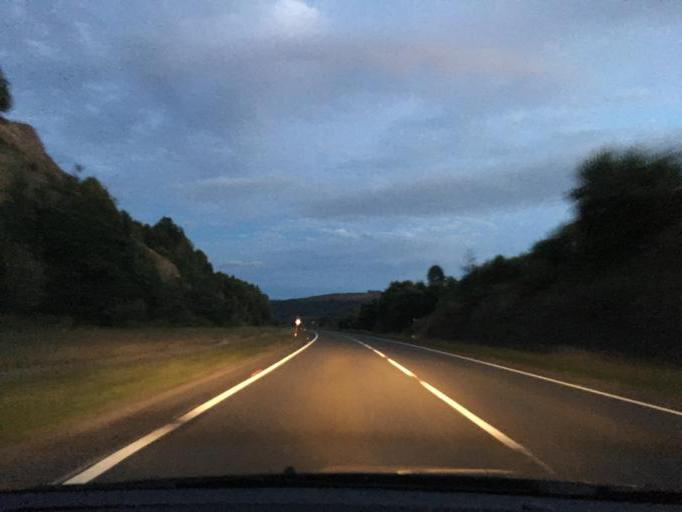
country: GB
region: Scotland
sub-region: Perth and Kinross
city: Aberfeldy
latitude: 56.7872
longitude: -4.0092
